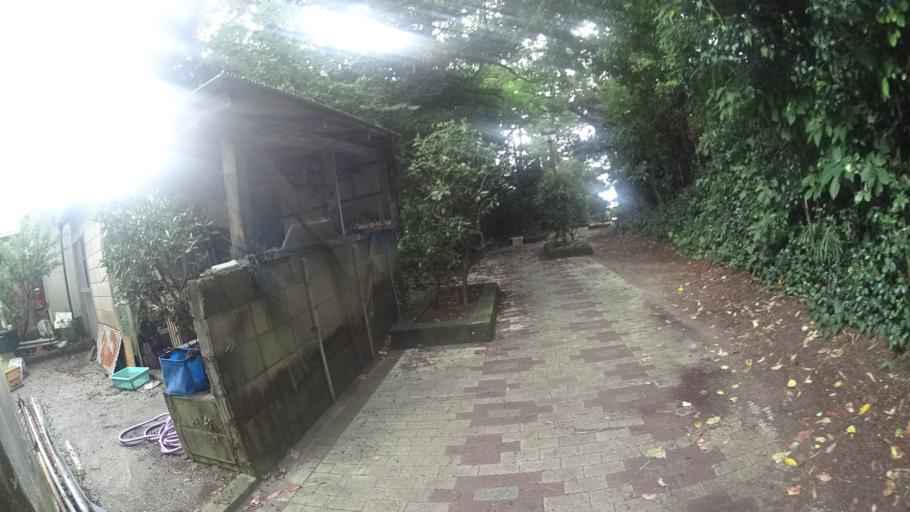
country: JP
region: Shizuoka
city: Shimoda
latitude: 34.3235
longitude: 139.2202
